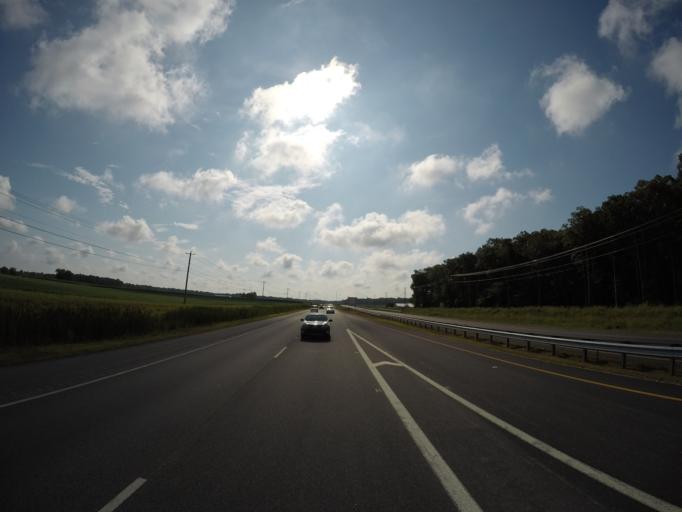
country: US
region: Maryland
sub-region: Caroline County
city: Ridgely
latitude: 38.9287
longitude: -76.0034
